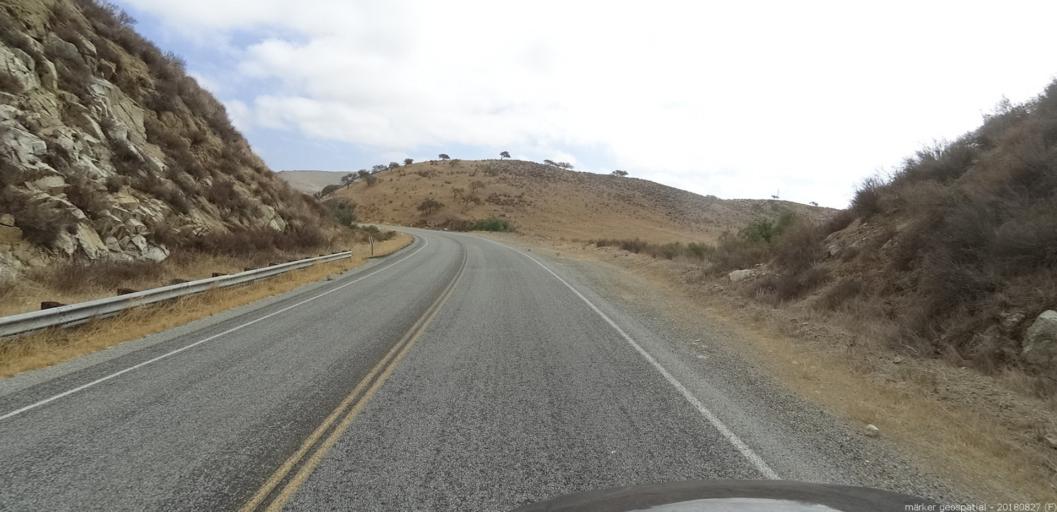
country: US
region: California
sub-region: Monterey County
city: King City
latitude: 36.2682
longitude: -121.0673
